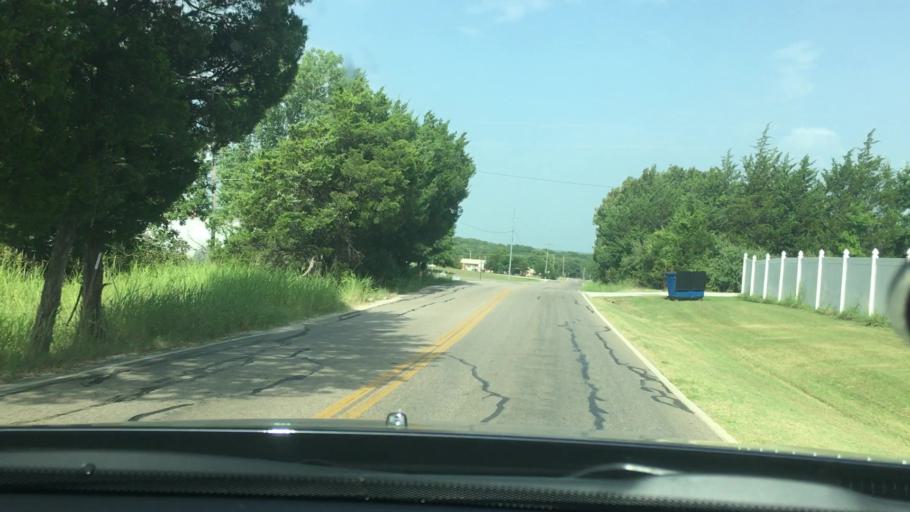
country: US
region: Oklahoma
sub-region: Pontotoc County
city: Byng
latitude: 34.8685
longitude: -96.6704
